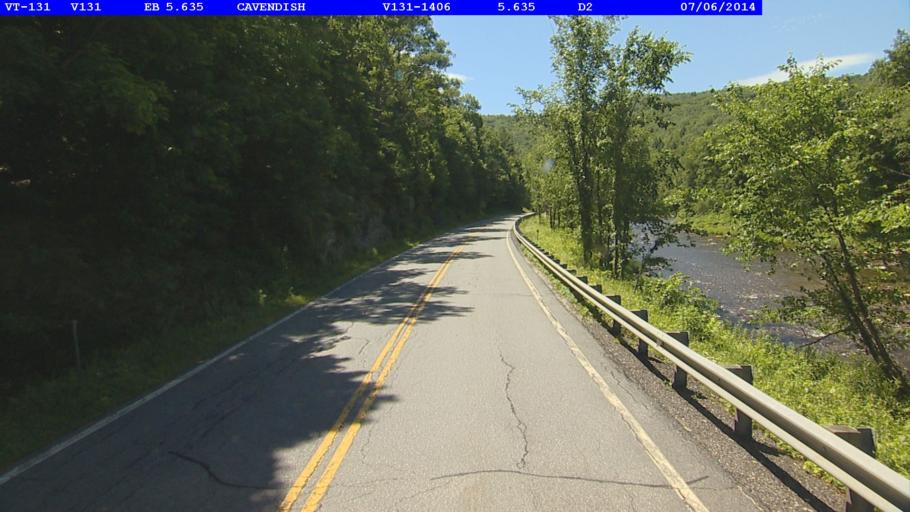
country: US
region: Vermont
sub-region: Windsor County
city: Springfield
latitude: 43.3945
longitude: -72.5680
